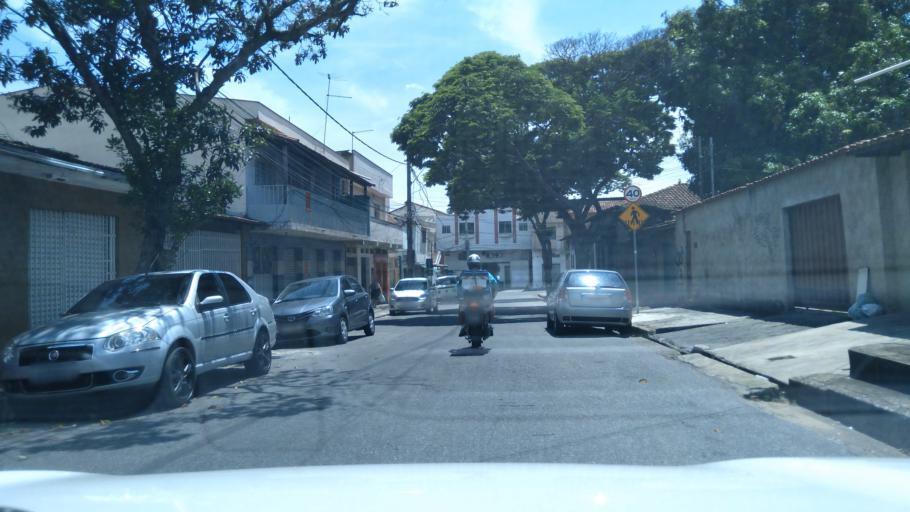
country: BR
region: Minas Gerais
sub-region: Contagem
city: Contagem
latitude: -19.8964
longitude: -44.0118
